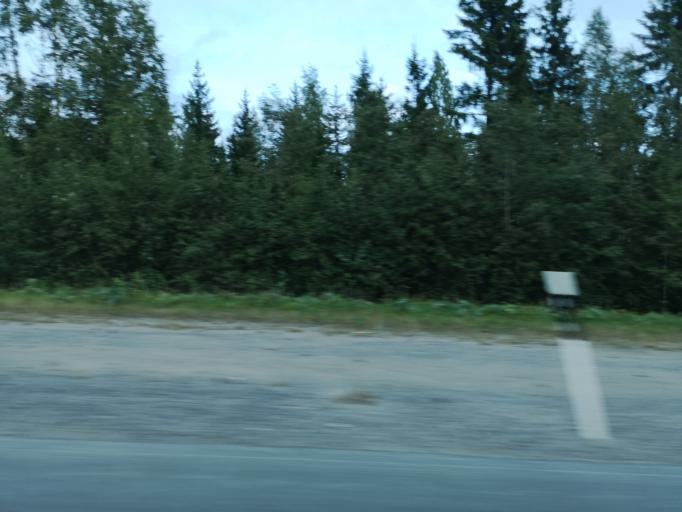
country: FI
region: Central Finland
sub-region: Joutsa
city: Joutsa
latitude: 61.7679
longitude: 26.1027
